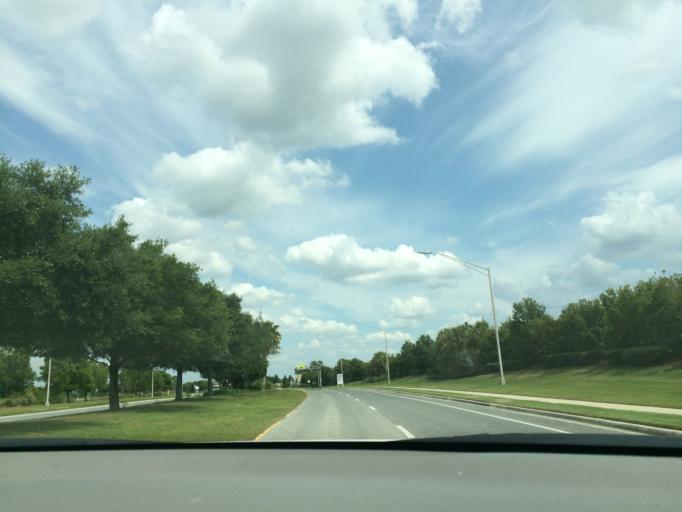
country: US
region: Florida
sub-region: Sarasota County
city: The Meadows
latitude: 27.4590
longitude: -82.4257
